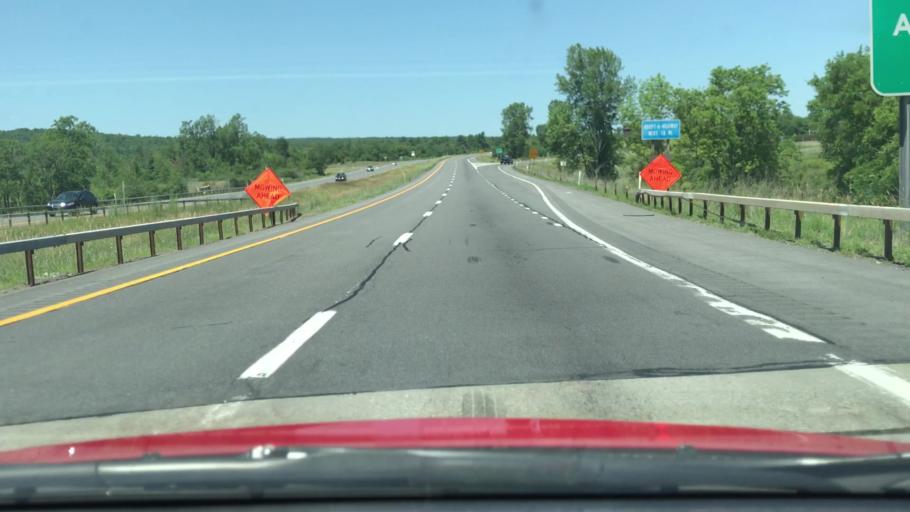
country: US
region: New York
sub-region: Essex County
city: Keeseville
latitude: 44.4915
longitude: -73.4948
